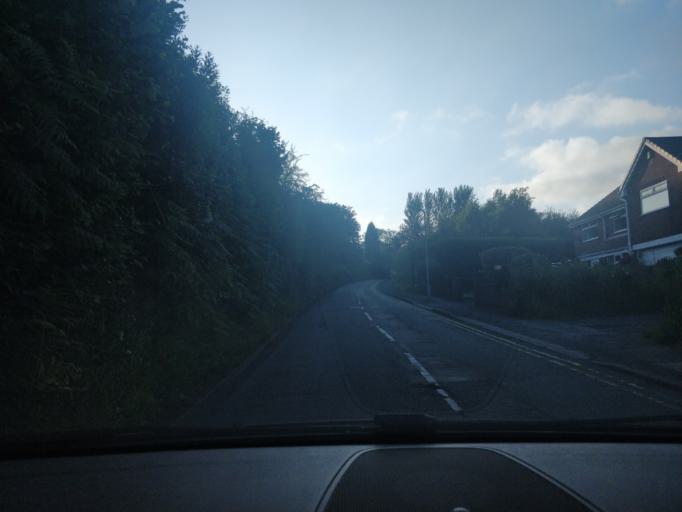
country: GB
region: England
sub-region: Lancashire
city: Appley Bridge
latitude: 53.5452
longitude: -2.7346
